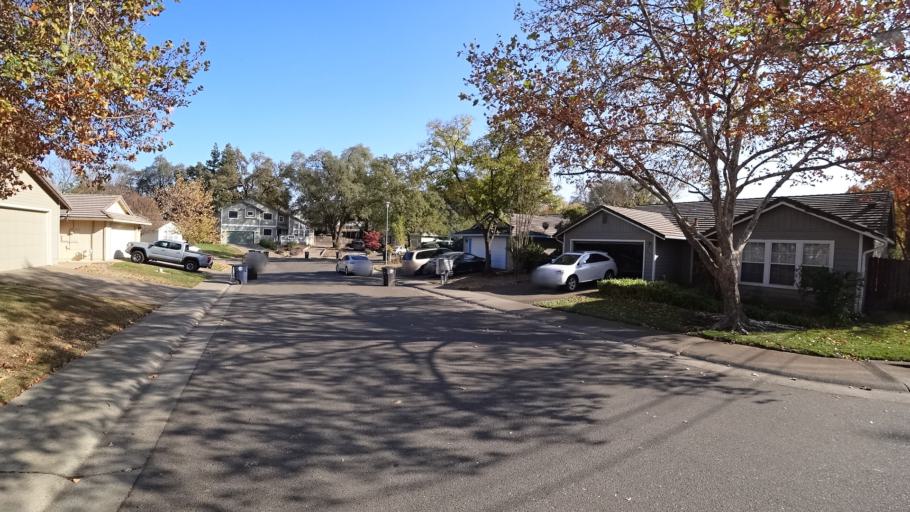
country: US
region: California
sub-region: Sacramento County
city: Citrus Heights
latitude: 38.6905
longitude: -121.2762
